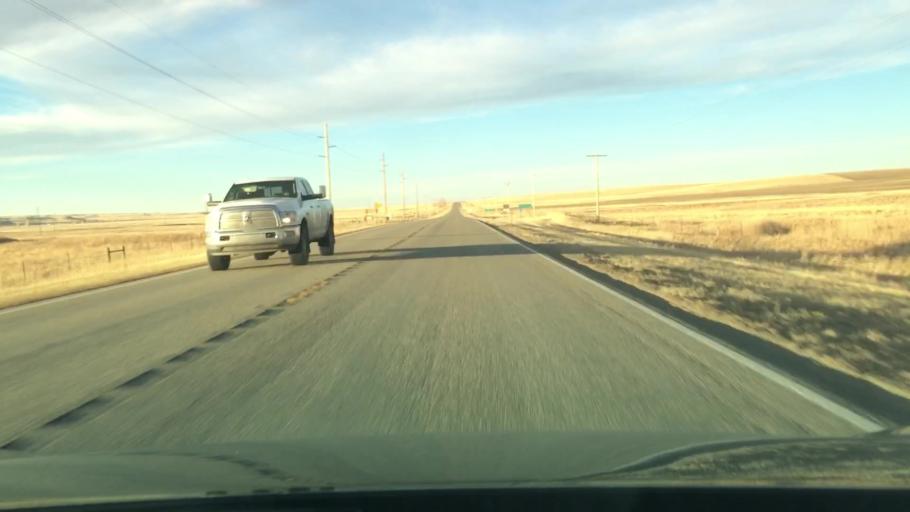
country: US
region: Montana
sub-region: Wheatland County
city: Harlowton
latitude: 46.8217
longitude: -109.7607
